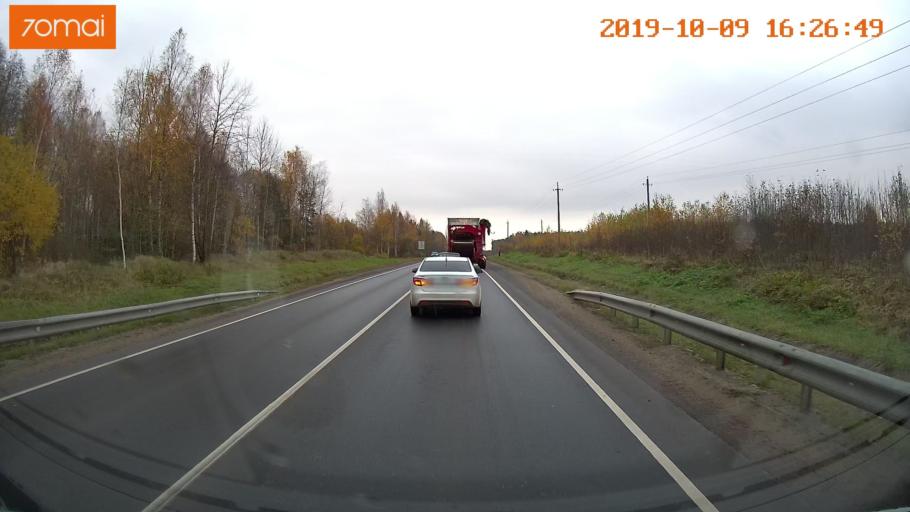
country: RU
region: Kostroma
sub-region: Kostromskoy Rayon
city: Kostroma
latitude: 57.6360
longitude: 40.9256
